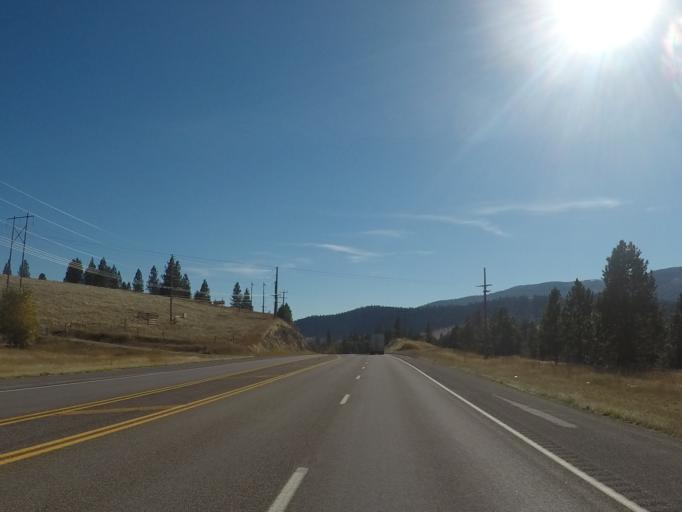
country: US
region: Montana
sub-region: Missoula County
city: Frenchtown
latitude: 47.1833
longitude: -114.1015
